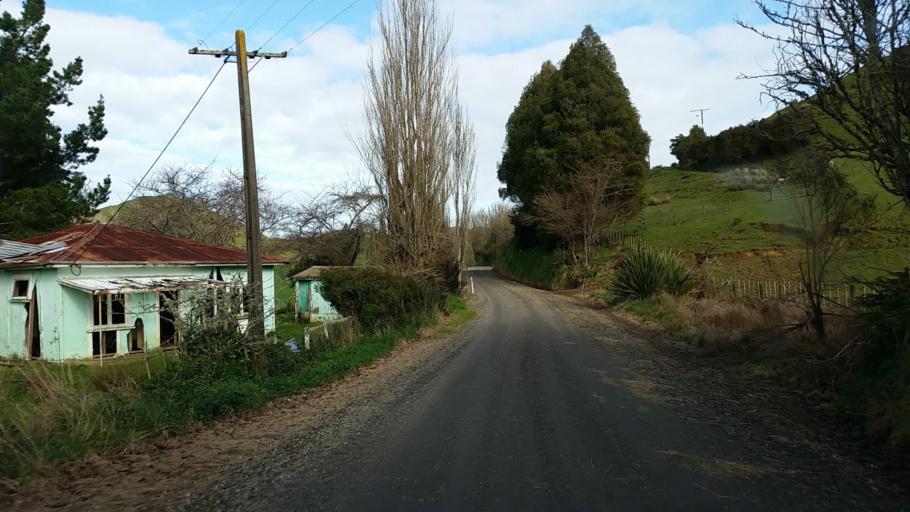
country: NZ
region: Taranaki
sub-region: South Taranaki District
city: Eltham
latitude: -39.2527
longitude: 174.5328
